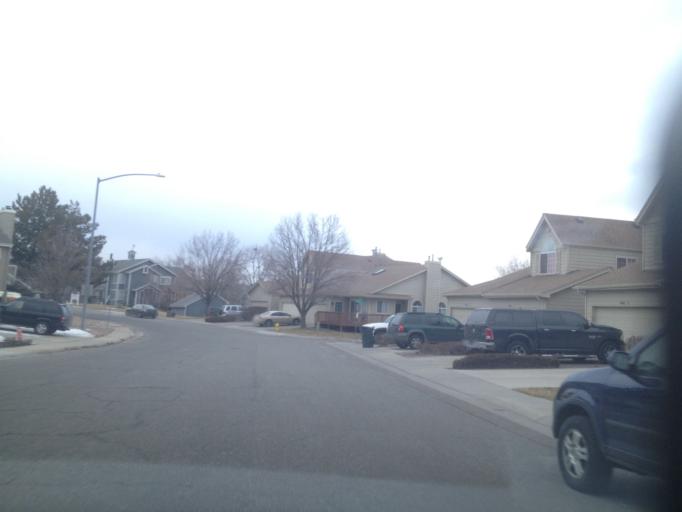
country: US
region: Colorado
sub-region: Adams County
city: Westminster
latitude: 39.8170
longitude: -105.0491
